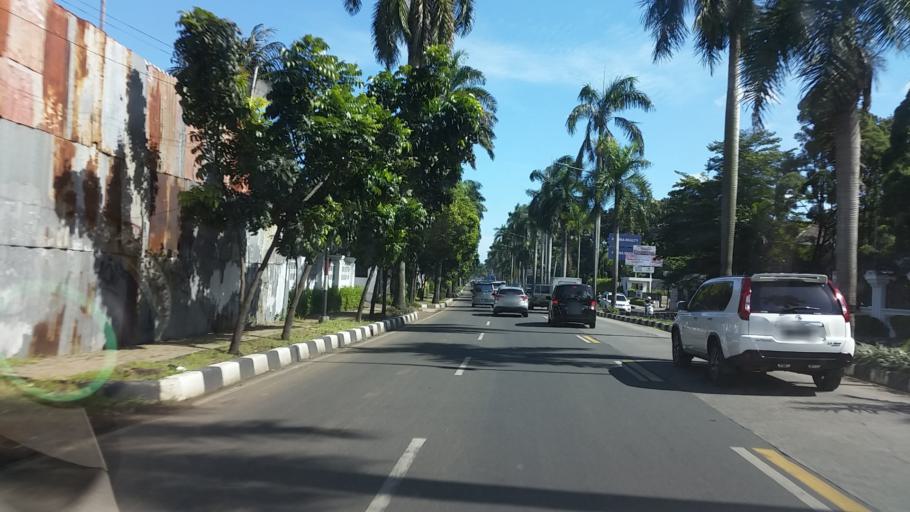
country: ID
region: Banten
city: South Tangerang
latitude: -6.2792
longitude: 106.7810
